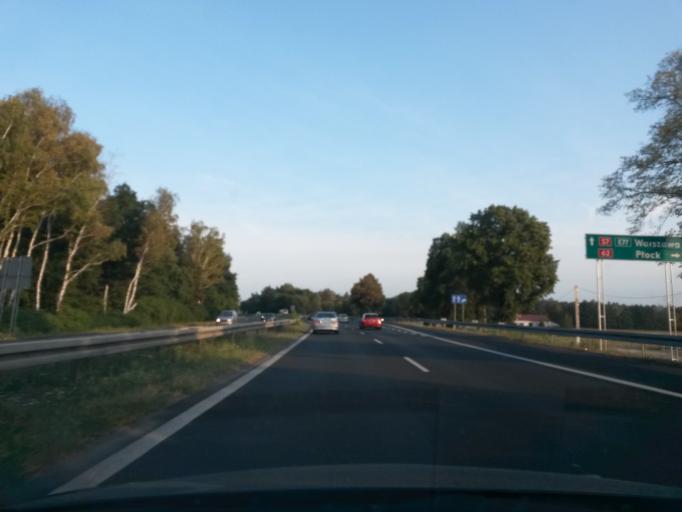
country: PL
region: Masovian Voivodeship
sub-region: Powiat nowodworski
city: Zakroczym
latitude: 52.4560
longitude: 20.5801
